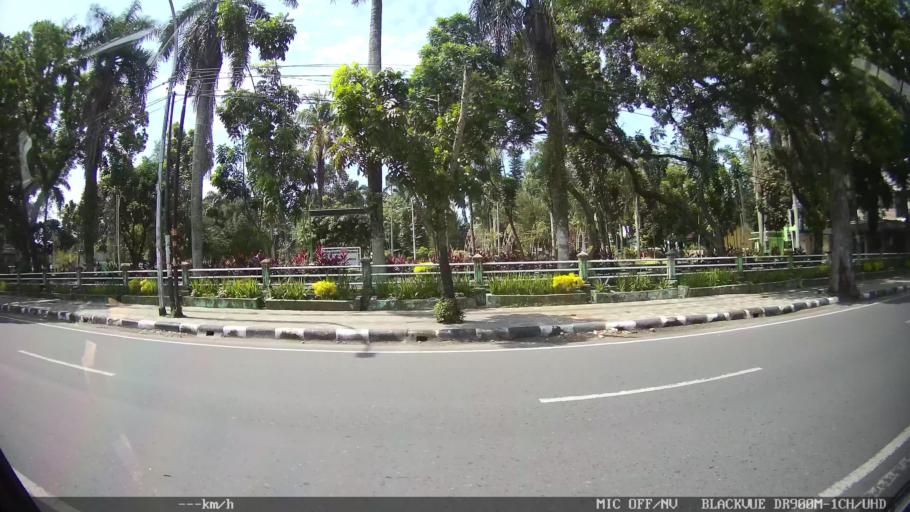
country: ID
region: North Sumatra
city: Medan
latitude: 3.5847
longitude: 98.6582
